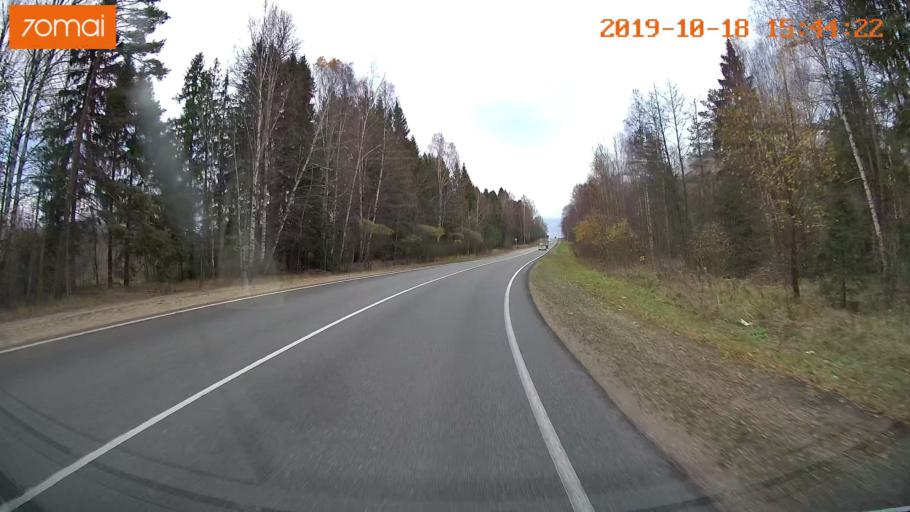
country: RU
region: Vladimir
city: Golovino
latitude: 55.9807
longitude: 40.5490
